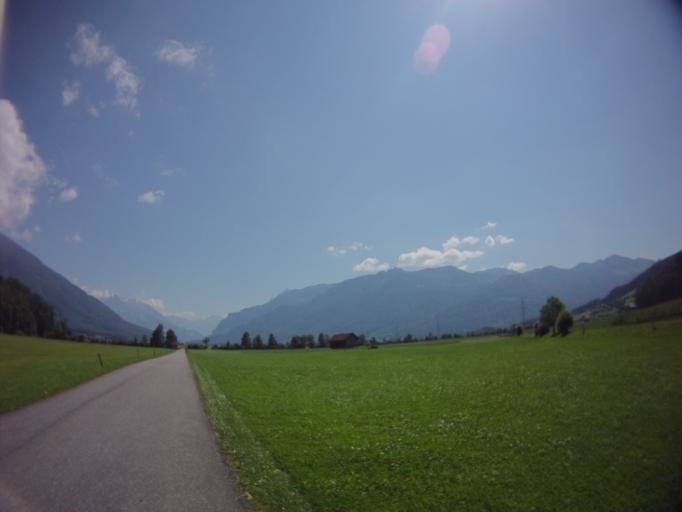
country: CH
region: Saint Gallen
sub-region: Wahlkreis See-Gaster
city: Kaltbrunn
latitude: 47.1932
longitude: 9.0339
